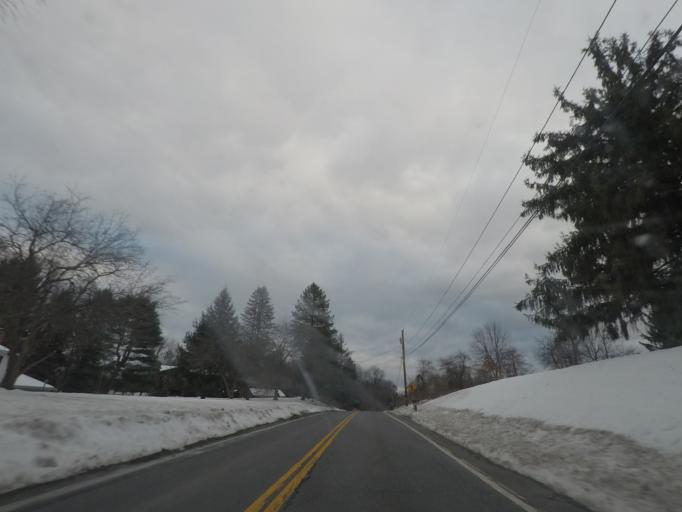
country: US
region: New York
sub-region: Ulster County
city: Clintondale
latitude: 41.6863
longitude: -74.1043
